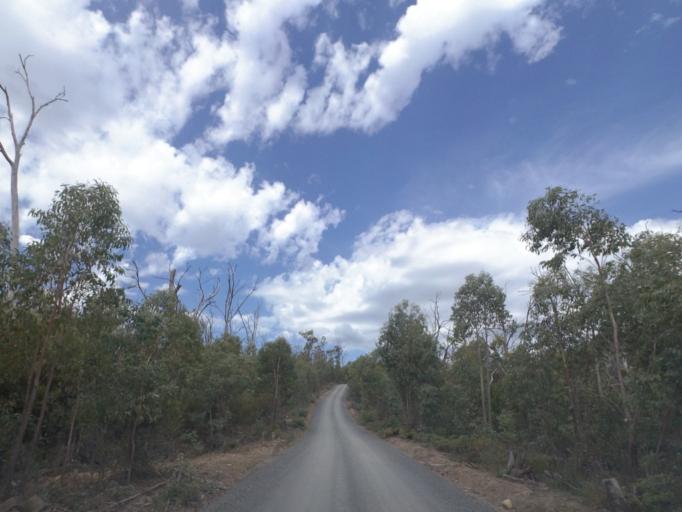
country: AU
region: Victoria
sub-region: Murrindindi
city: Alexandra
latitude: -37.3939
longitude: 145.7552
